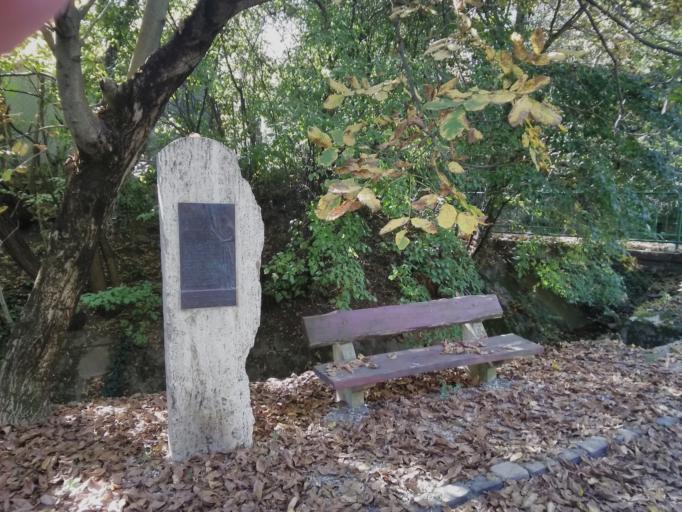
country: HU
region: Pest
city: Szentendre
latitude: 47.6891
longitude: 19.0829
